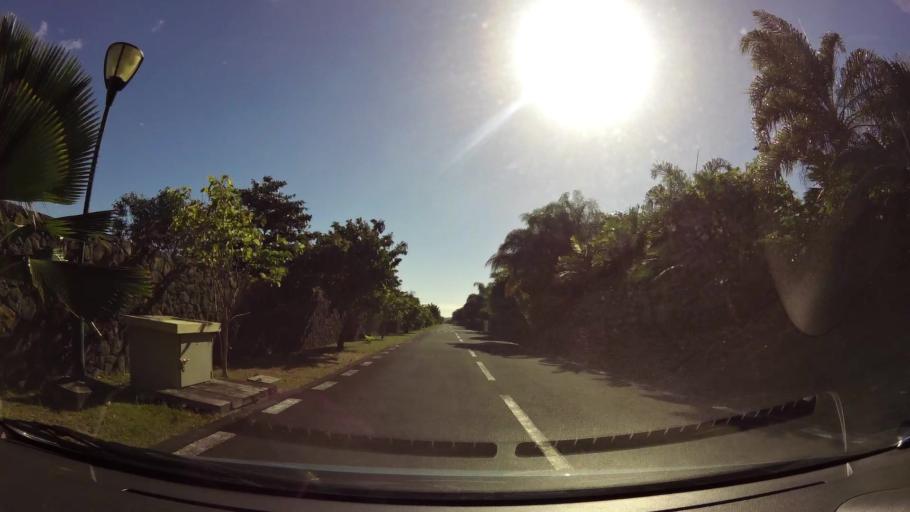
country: MU
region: Black River
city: Grande Riviere Noire
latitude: -20.3434
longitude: 57.3667
